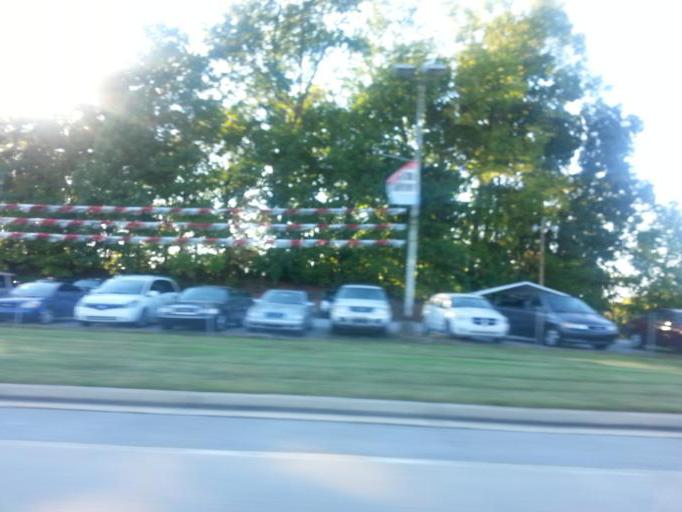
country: US
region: Tennessee
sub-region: Blount County
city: Alcoa
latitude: 35.8332
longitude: -83.9726
